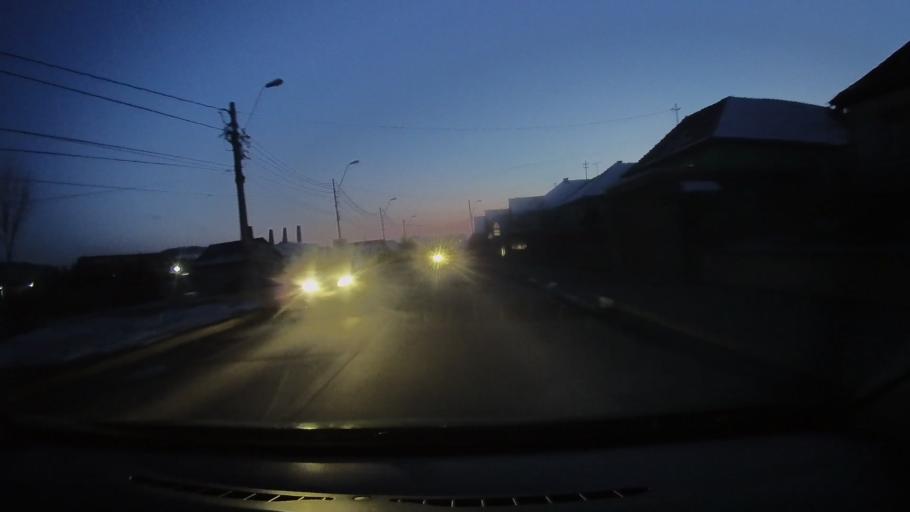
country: RO
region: Sibiu
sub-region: Municipiul Medias
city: Medias
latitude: 46.1758
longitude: 24.3633
